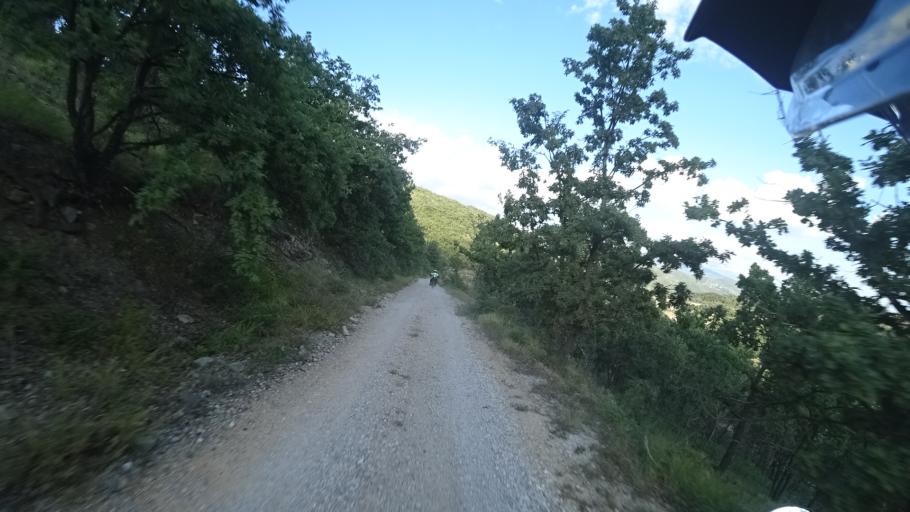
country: HR
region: Sibensko-Kniniska
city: Knin
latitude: 44.1361
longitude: 16.1243
